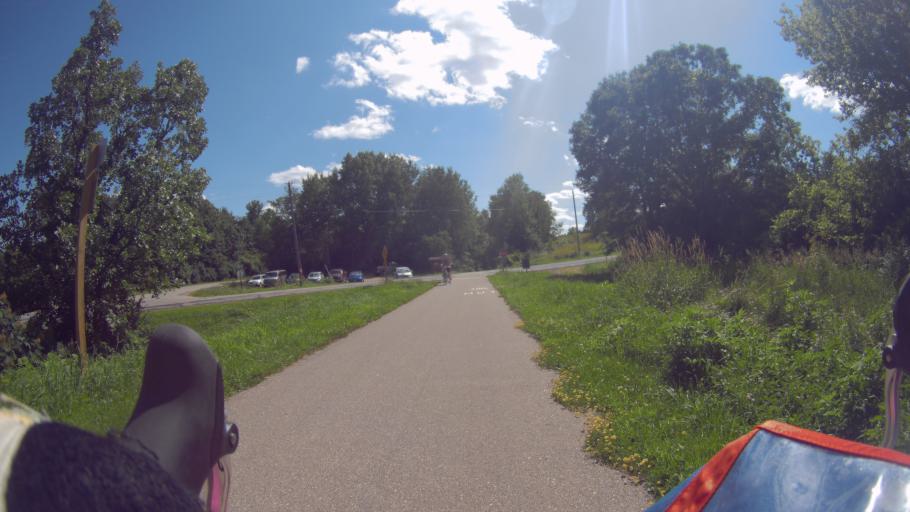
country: US
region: Wisconsin
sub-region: Dane County
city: Fitchburg
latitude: 42.9435
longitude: -89.4818
